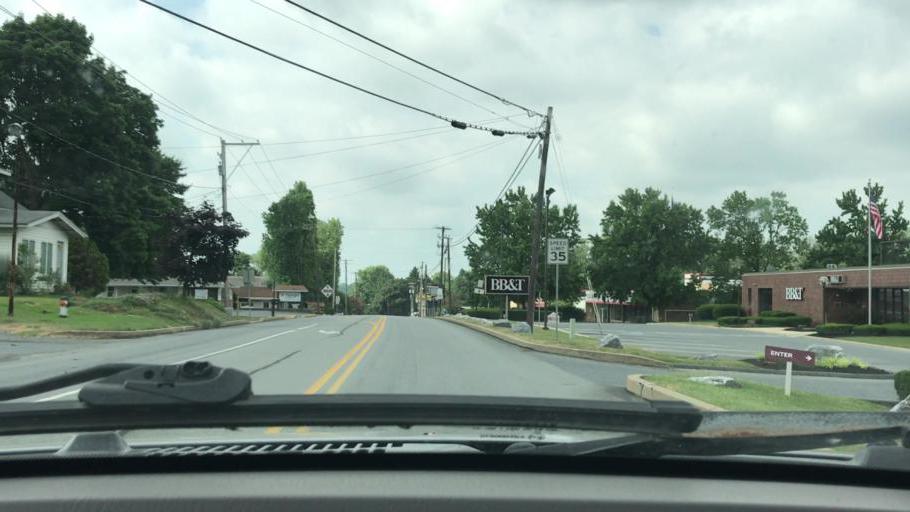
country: US
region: Pennsylvania
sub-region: Lancaster County
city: Elizabethtown
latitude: 40.1651
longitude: -76.6081
